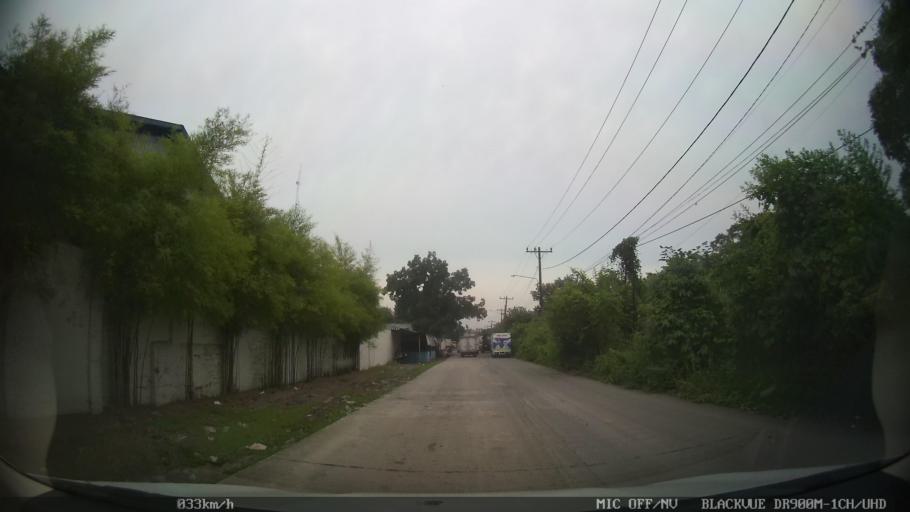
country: ID
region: North Sumatra
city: Deli Tua
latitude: 3.5356
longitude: 98.7261
